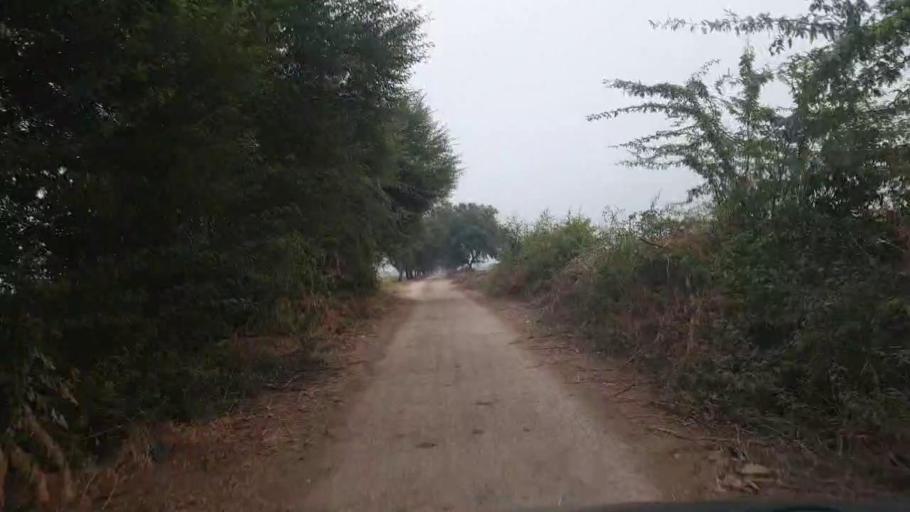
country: PK
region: Sindh
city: Tando Adam
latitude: 25.8478
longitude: 68.6880
